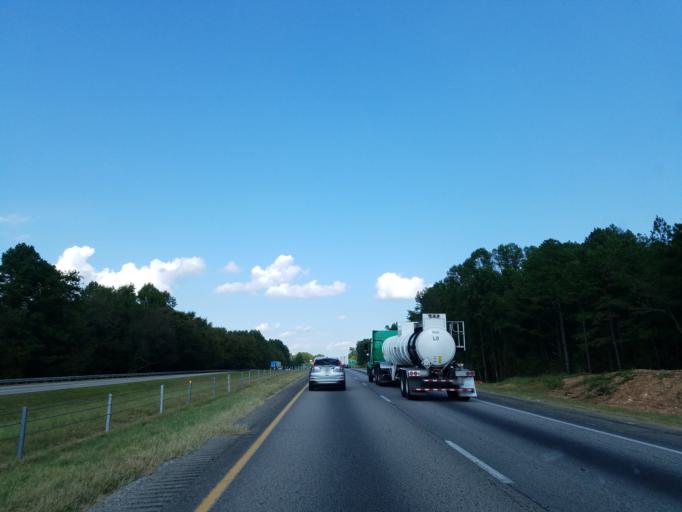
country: US
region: Georgia
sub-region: Jackson County
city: Jefferson
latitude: 34.1733
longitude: -83.6136
